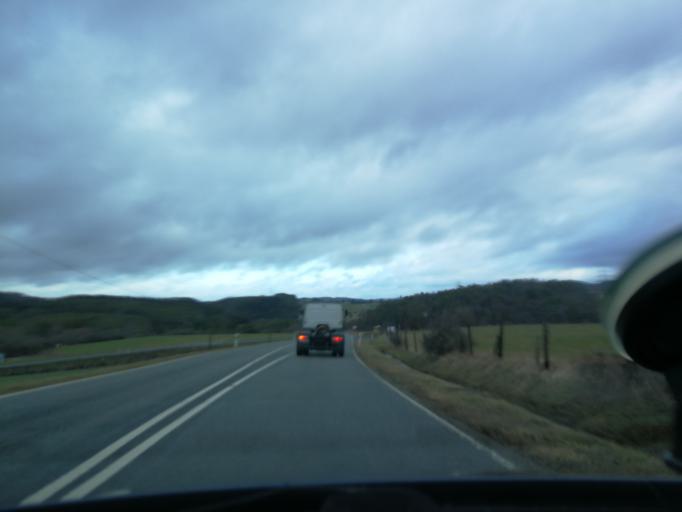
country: DE
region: Rheinland-Pfalz
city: Nohn
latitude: 50.3118
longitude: 6.7726
